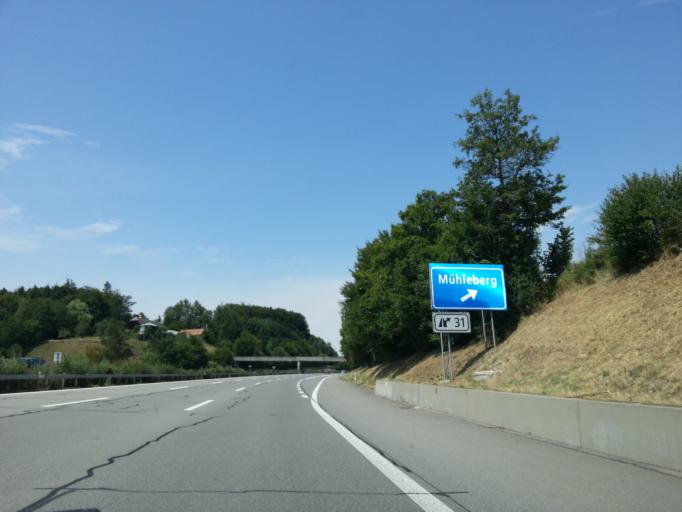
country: CH
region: Bern
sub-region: Bern-Mittelland District
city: Frauenkappelen
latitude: 46.9506
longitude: 7.3300
